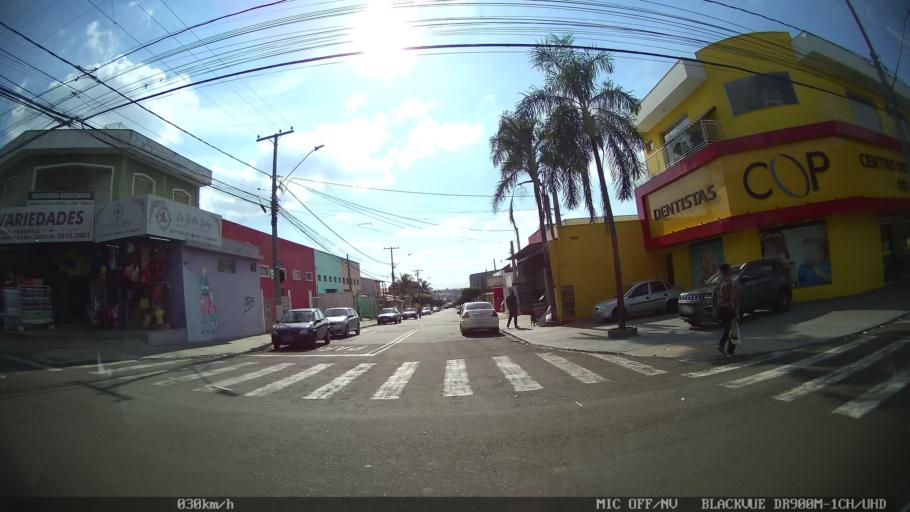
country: BR
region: Sao Paulo
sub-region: Hortolandia
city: Hortolandia
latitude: -22.9016
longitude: -47.2398
